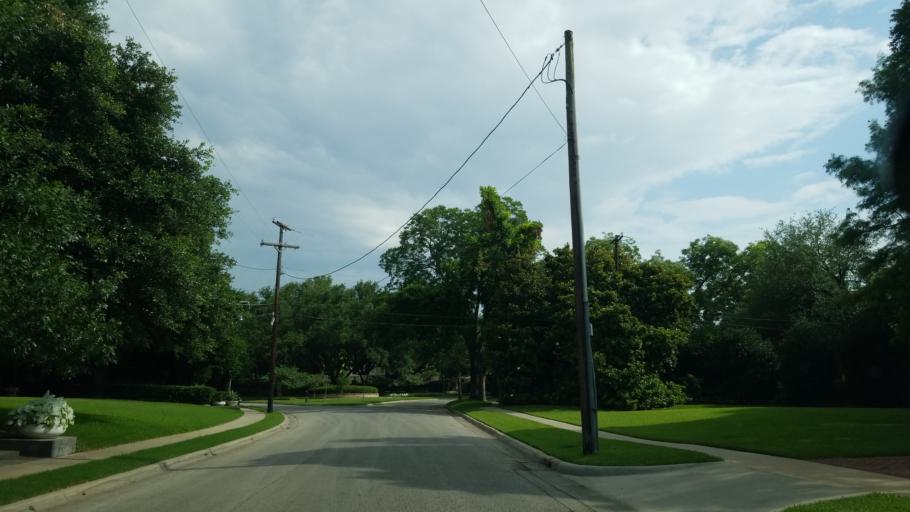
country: US
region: Texas
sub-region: Dallas County
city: University Park
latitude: 32.8494
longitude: -96.8016
